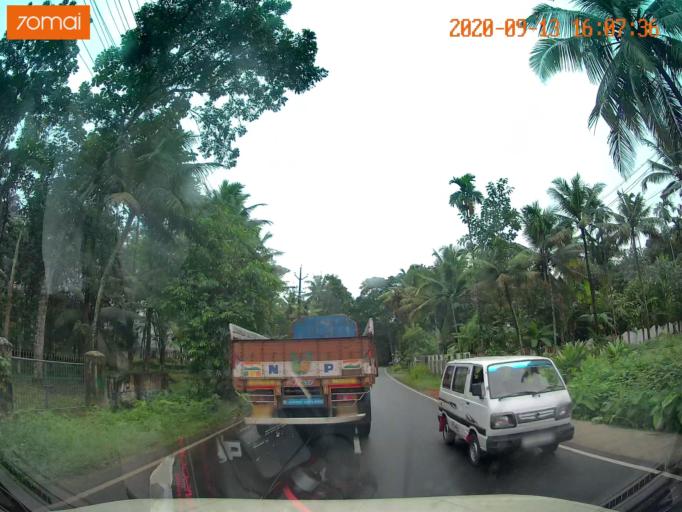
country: IN
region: Kerala
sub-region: Kottayam
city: Palackattumala
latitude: 9.6748
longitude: 76.5867
